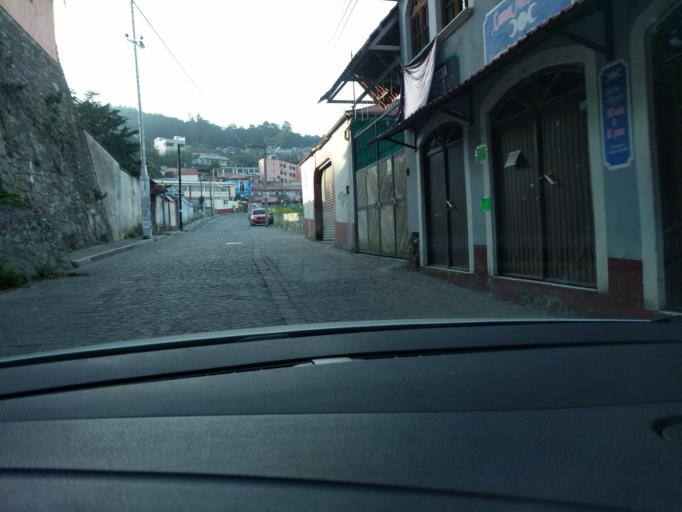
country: MX
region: Hidalgo
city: Mineral del Monte
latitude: 20.1413
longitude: -98.6726
